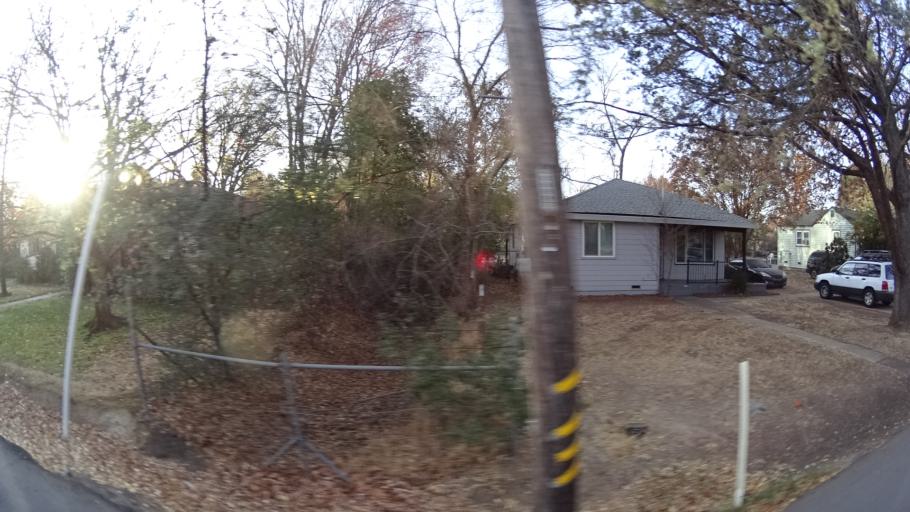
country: US
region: California
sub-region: Sacramento County
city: Citrus Heights
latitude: 38.7185
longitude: -121.2796
